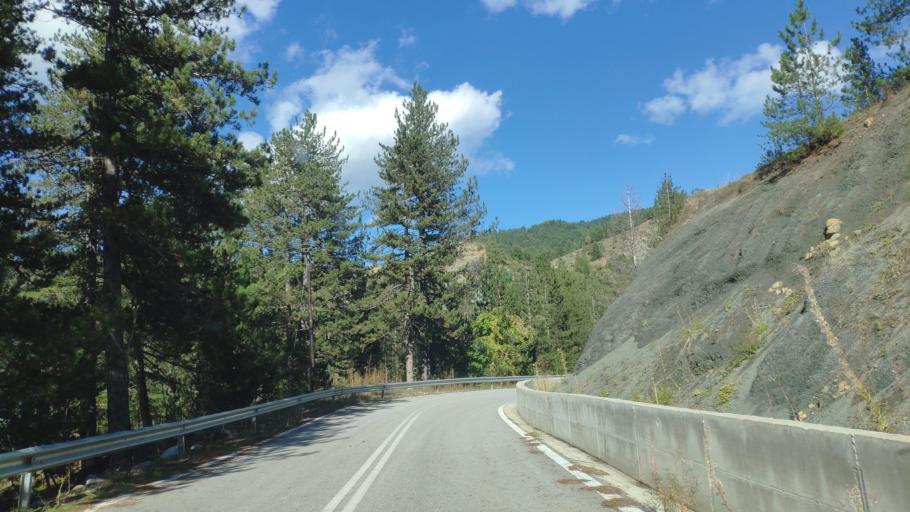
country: AL
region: Korce
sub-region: Rrethi i Devollit
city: Miras
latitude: 40.4096
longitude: 20.8752
